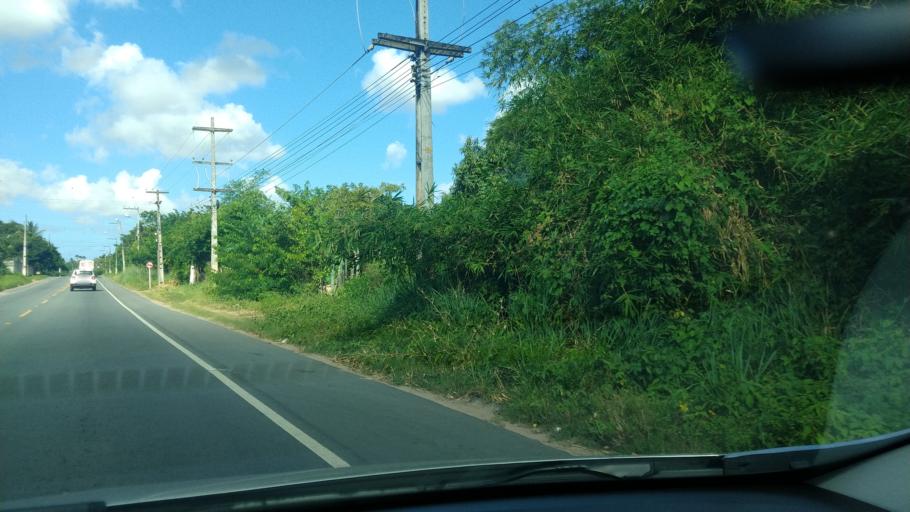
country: BR
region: Rio Grande do Norte
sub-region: Sao Goncalo Do Amarante
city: Sao Goncalo do Amarante
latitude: -5.7891
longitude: -35.3204
